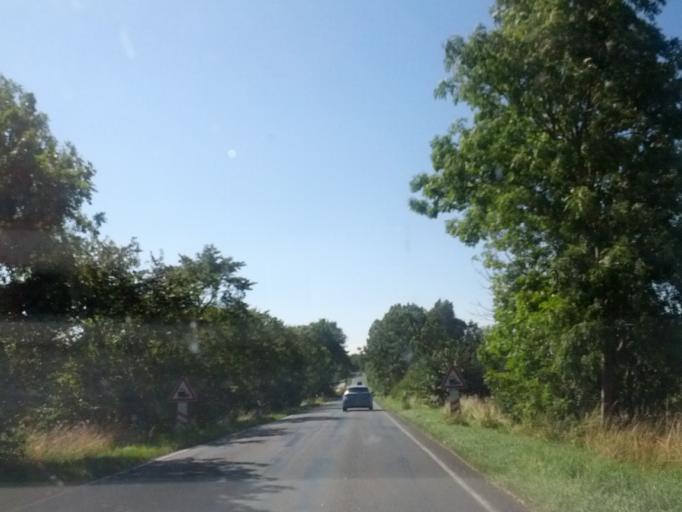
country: DE
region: Mecklenburg-Vorpommern
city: Bergen auf Ruegen
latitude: 54.4364
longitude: 13.4355
